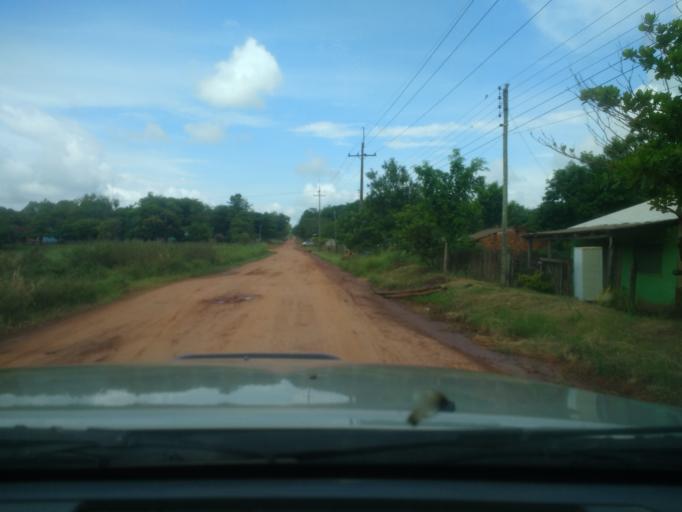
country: PY
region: San Pedro
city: Puerto Rosario
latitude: -24.4158
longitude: -57.1086
